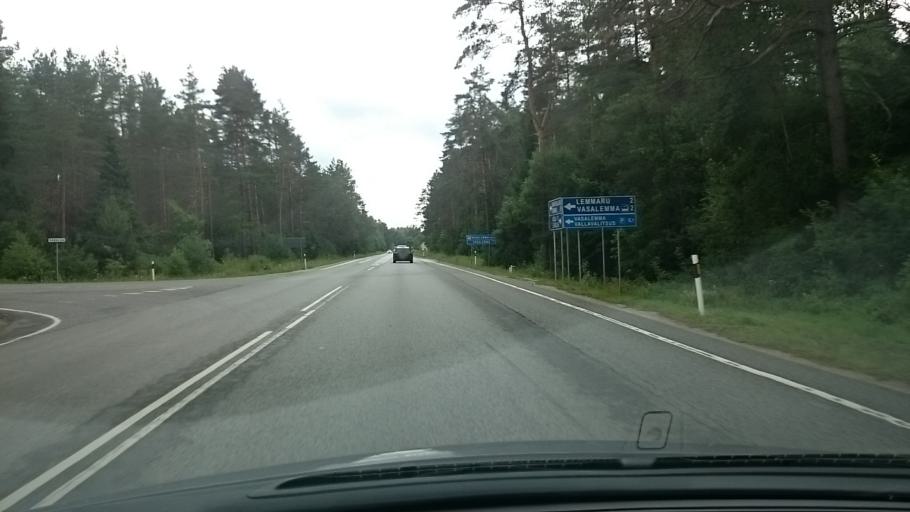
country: EE
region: Harju
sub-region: Nissi vald
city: Riisipere
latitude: 59.2443
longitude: 24.2782
